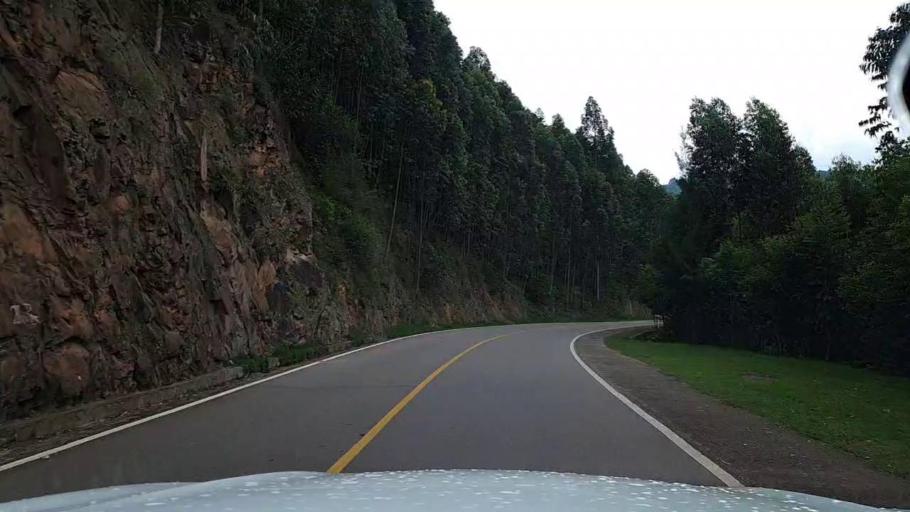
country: RW
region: Northern Province
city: Byumba
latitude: -1.7167
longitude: 30.1212
